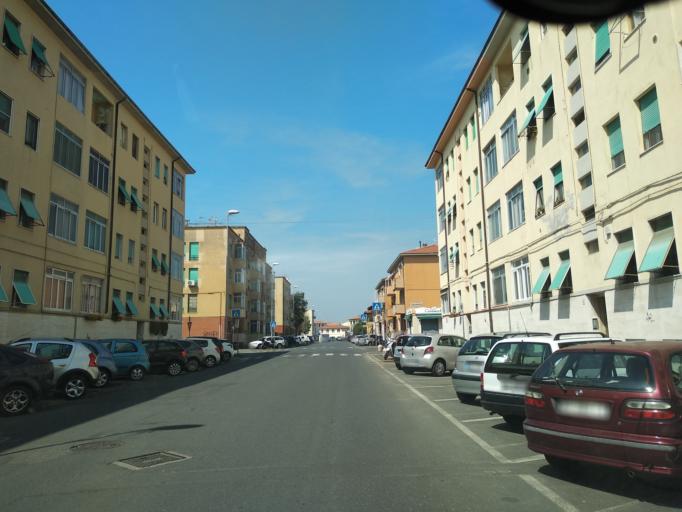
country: IT
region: Tuscany
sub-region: Provincia di Livorno
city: Livorno
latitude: 43.5609
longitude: 10.3319
